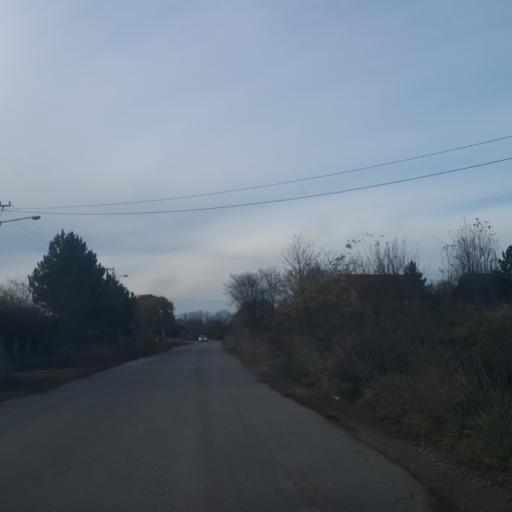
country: RS
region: Central Serbia
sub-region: Belgrade
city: Lazarevac
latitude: 44.4145
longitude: 20.3144
